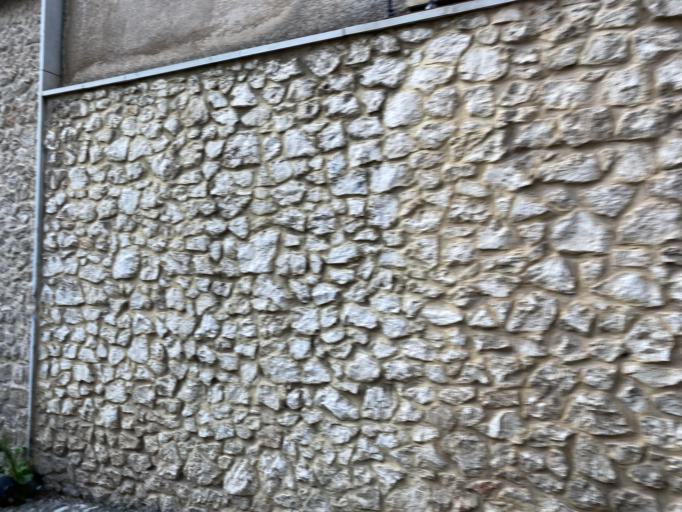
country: ES
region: Andalusia
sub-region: Provincia de Granada
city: Granada
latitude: 37.1800
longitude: -3.5977
